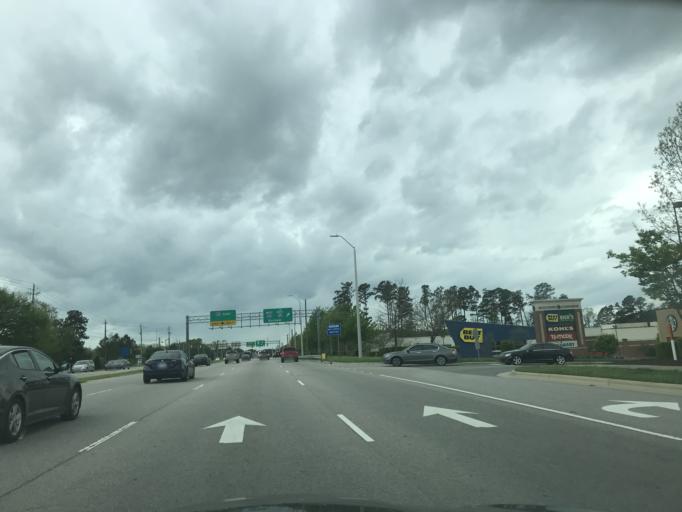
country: US
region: North Carolina
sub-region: Wake County
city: Knightdale
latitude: 35.7959
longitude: -78.5109
